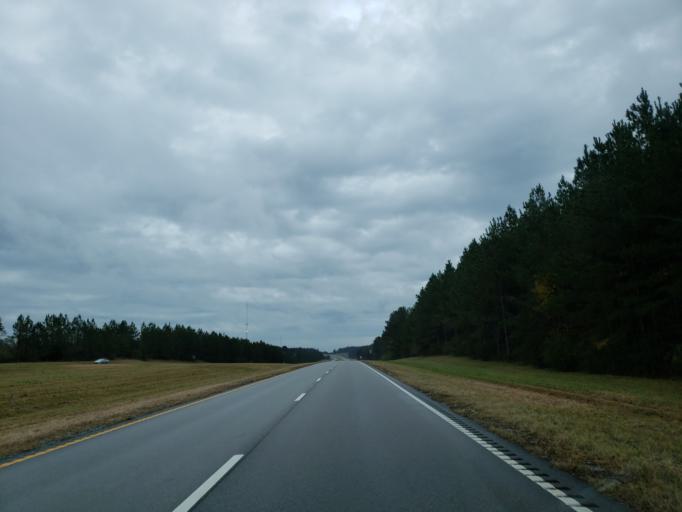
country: US
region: Mississippi
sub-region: Wayne County
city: Waynesboro
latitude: 31.6926
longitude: -88.7154
